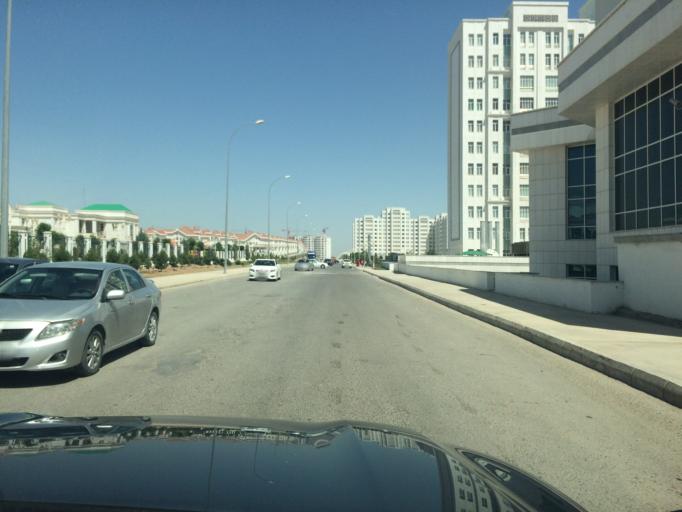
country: TM
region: Ahal
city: Ashgabat
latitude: 37.9292
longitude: 58.3670
